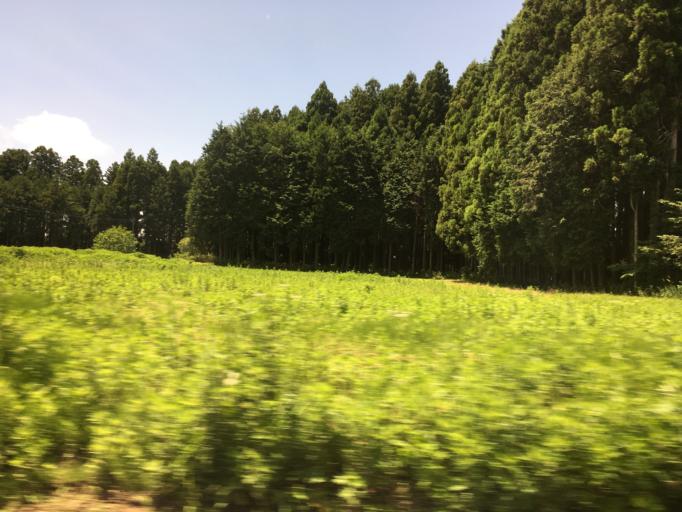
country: JP
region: Fukushima
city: Namie
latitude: 37.5061
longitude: 140.9843
